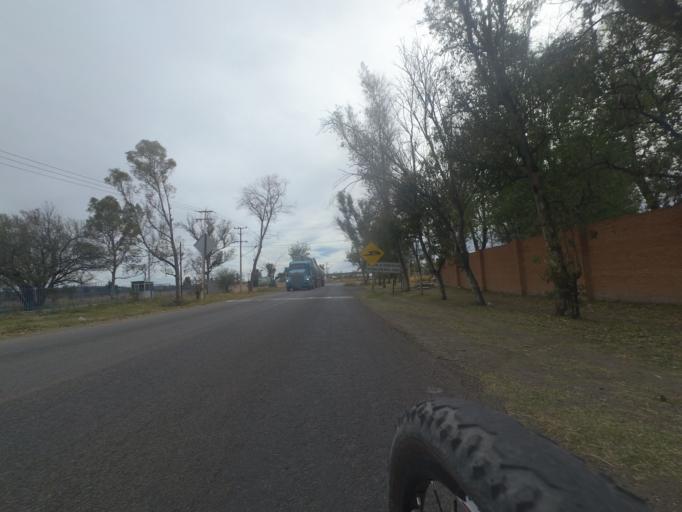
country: MX
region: Aguascalientes
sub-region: Aguascalientes
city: La Loma de los Negritos
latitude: 21.8387
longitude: -102.3550
